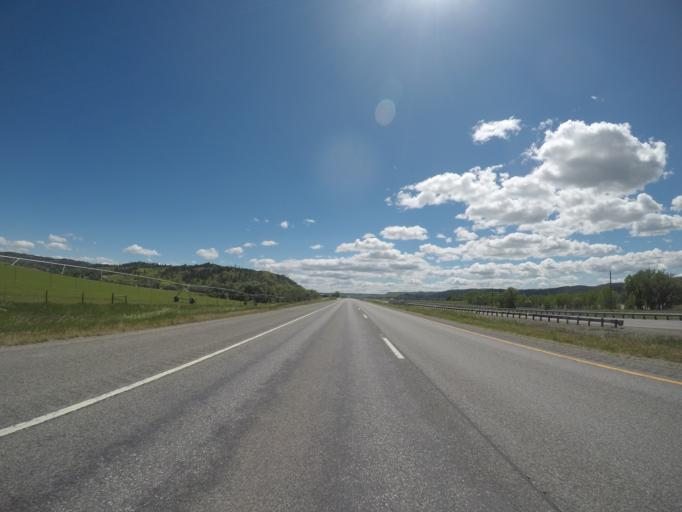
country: US
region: Montana
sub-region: Stillwater County
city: Columbus
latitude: 45.6053
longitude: -109.1630
